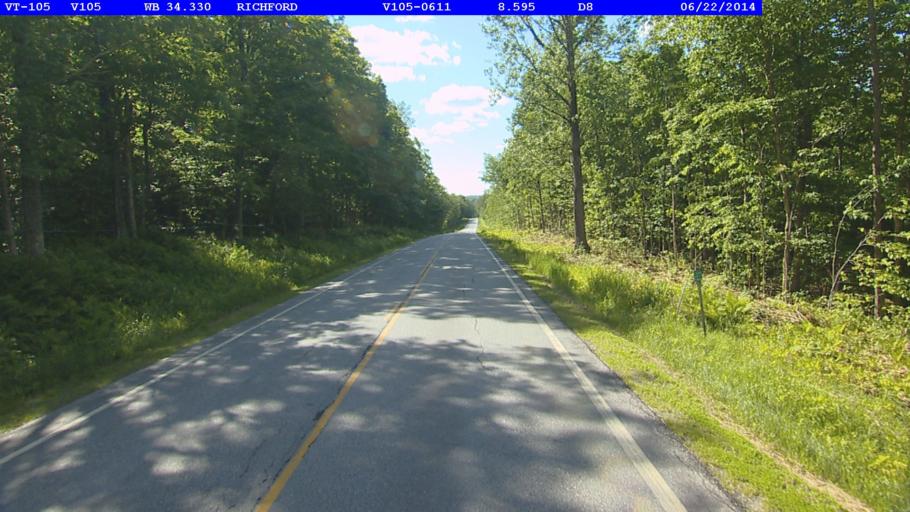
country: US
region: Vermont
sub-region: Franklin County
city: Richford
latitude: 44.9904
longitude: -72.5605
